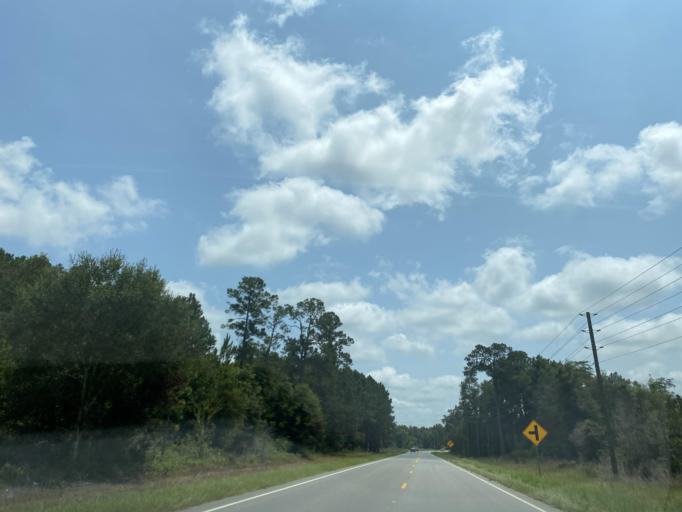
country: US
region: Georgia
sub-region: Jeff Davis County
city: Hazlehurst
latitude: 31.8091
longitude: -82.5664
